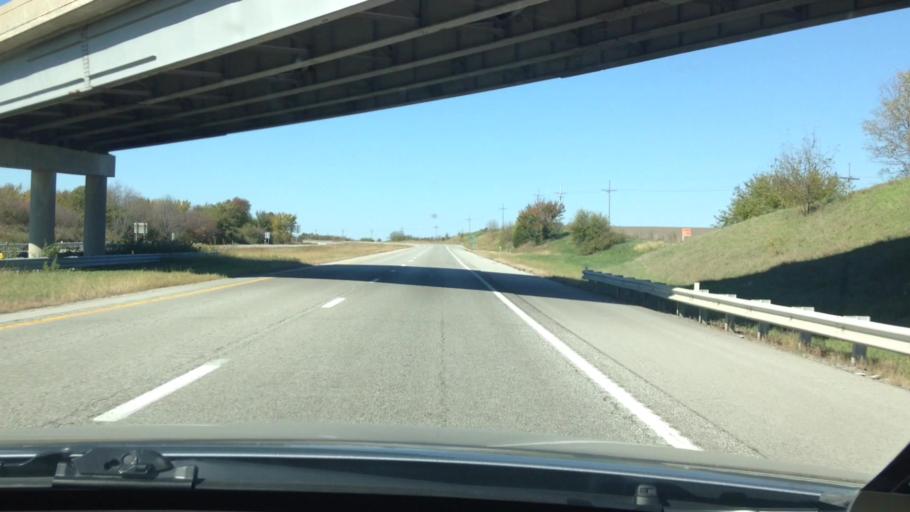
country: US
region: Missouri
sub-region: Platte County
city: Weatherby Lake
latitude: 39.3120
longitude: -94.6733
